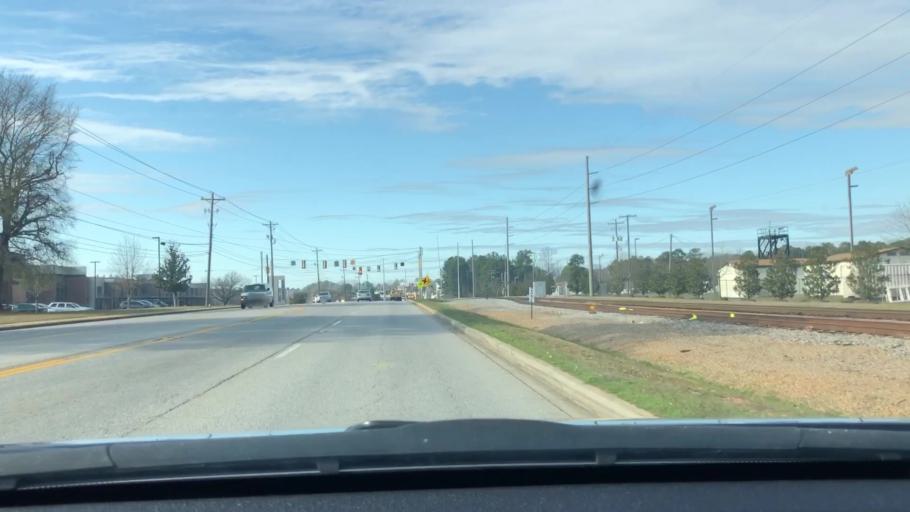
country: US
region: South Carolina
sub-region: Lexington County
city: Irmo
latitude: 34.0679
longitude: -81.1712
